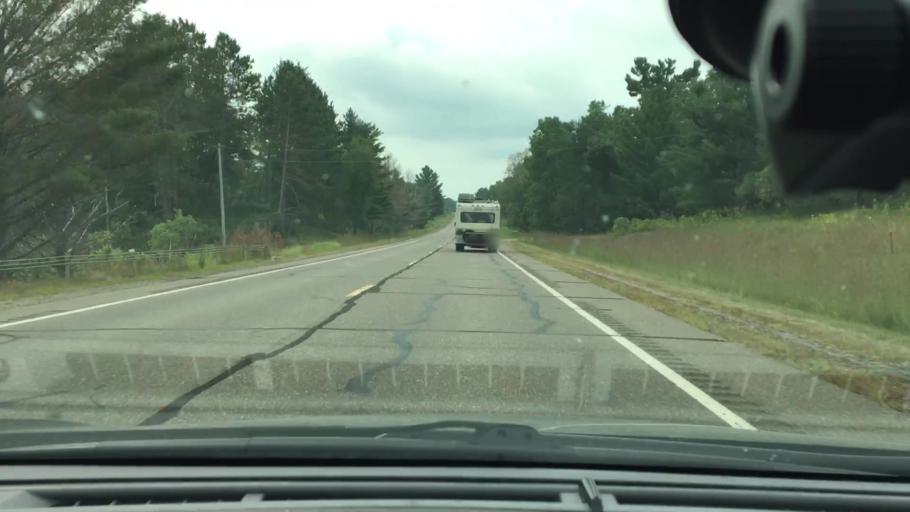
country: US
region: Minnesota
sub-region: Crow Wing County
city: Crosby
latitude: 46.4217
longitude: -93.8732
